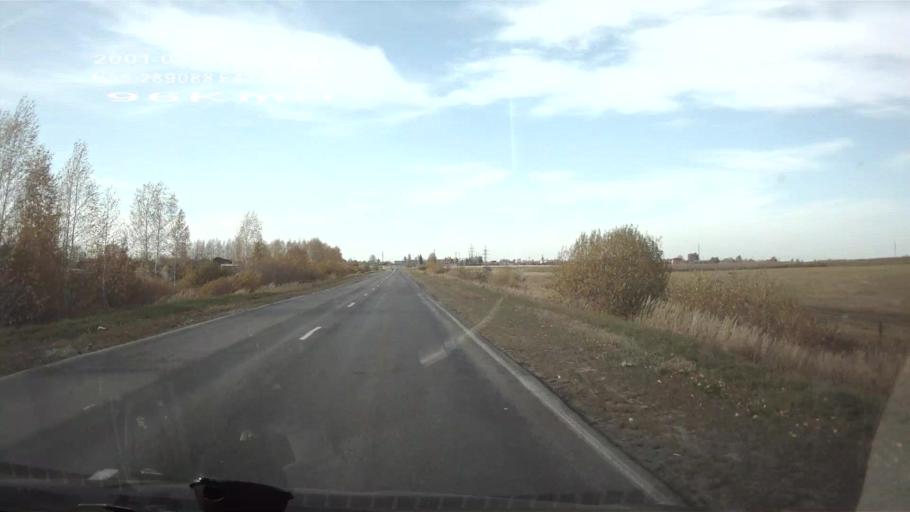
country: RU
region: Chuvashia
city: Ibresi
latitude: 55.2891
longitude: 47.0670
